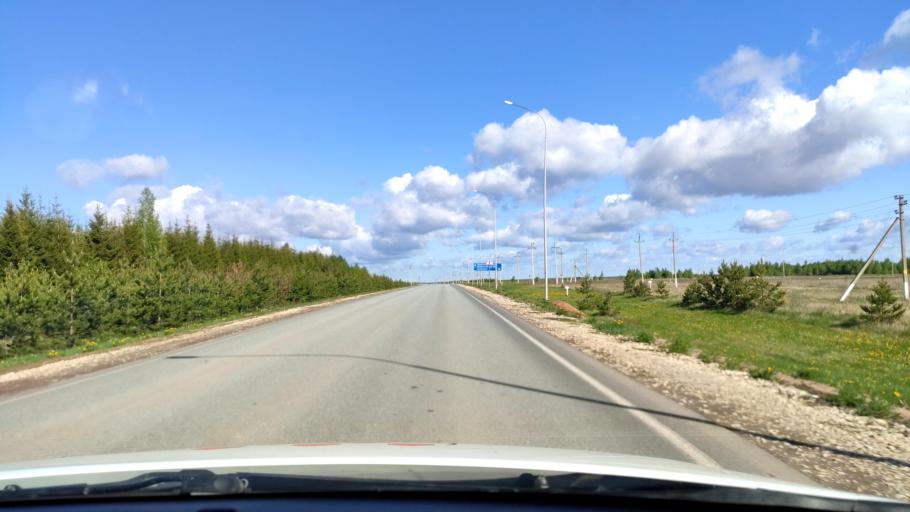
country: RU
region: Tatarstan
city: Sviyazhsk
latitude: 55.7357
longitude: 48.7383
